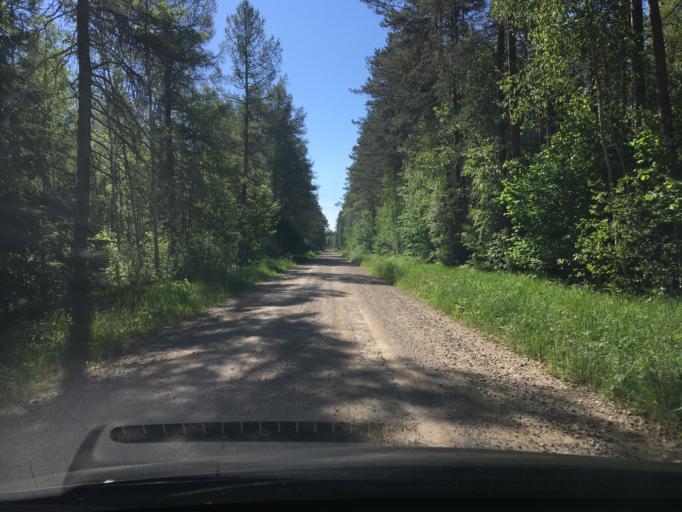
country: EE
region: Laeaene
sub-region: Lihula vald
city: Lihula
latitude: 58.6368
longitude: 23.7949
